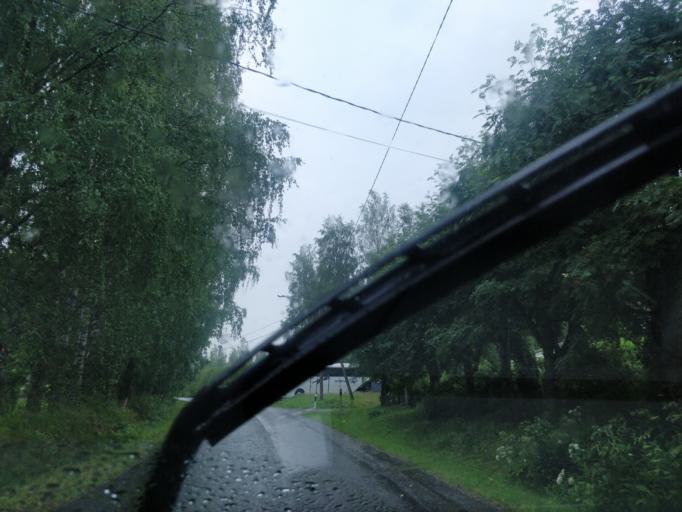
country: FI
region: Southern Savonia
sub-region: Mikkeli
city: Pertunmaa
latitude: 61.4259
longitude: 26.4239
